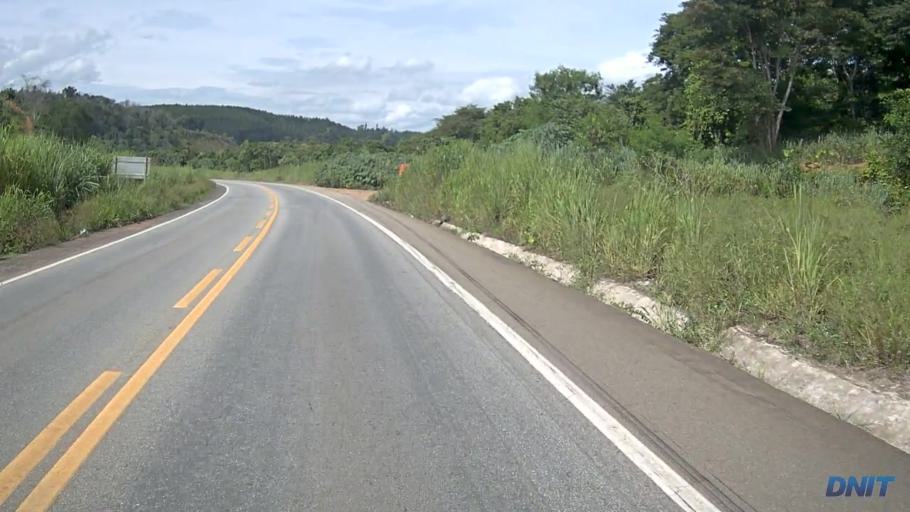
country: BR
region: Minas Gerais
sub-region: Ipaba
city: Ipaba
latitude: -19.3902
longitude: -42.4781
